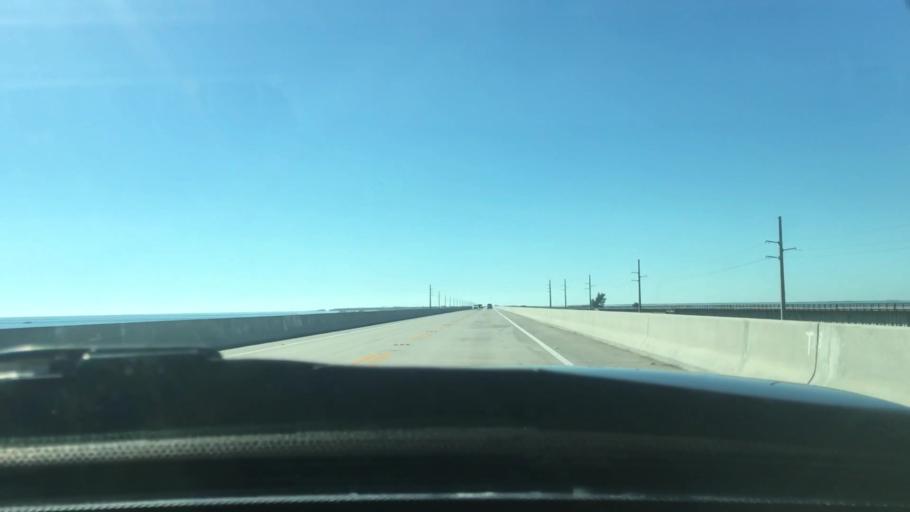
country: US
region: Florida
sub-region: Monroe County
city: Marathon
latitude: 24.6905
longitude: -81.1994
